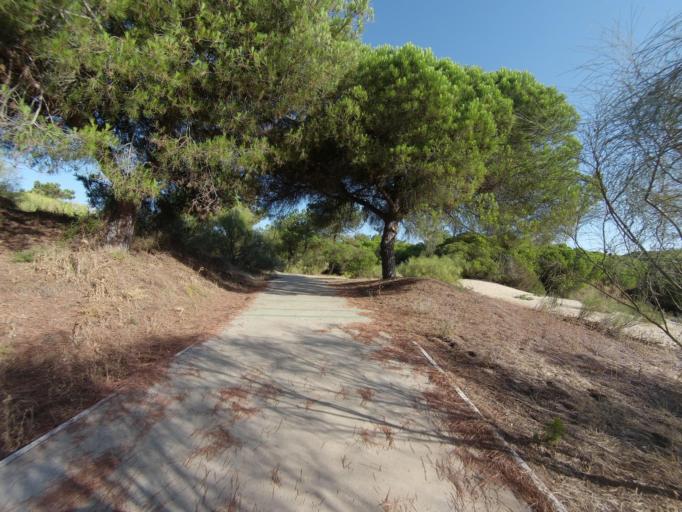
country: ES
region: Andalusia
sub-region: Provincia de Huelva
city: Aljaraque
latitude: 37.2095
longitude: -7.0391
